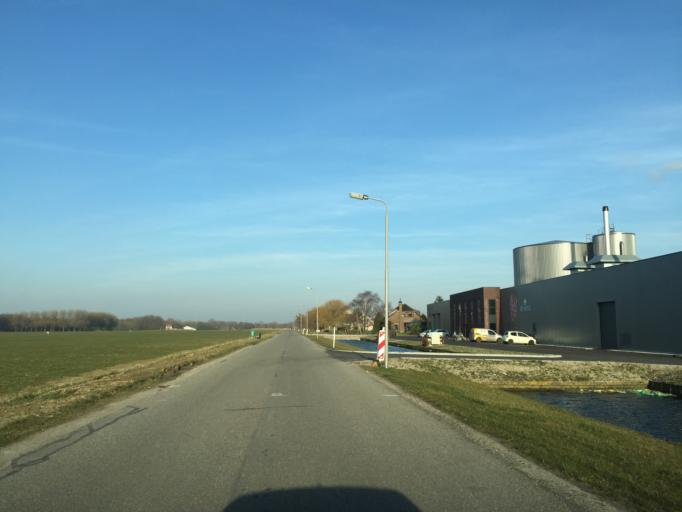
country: NL
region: South Holland
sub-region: Gemeente Pijnacker-Nootdorp
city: Pijnacker
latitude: 52.0177
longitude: 4.3977
